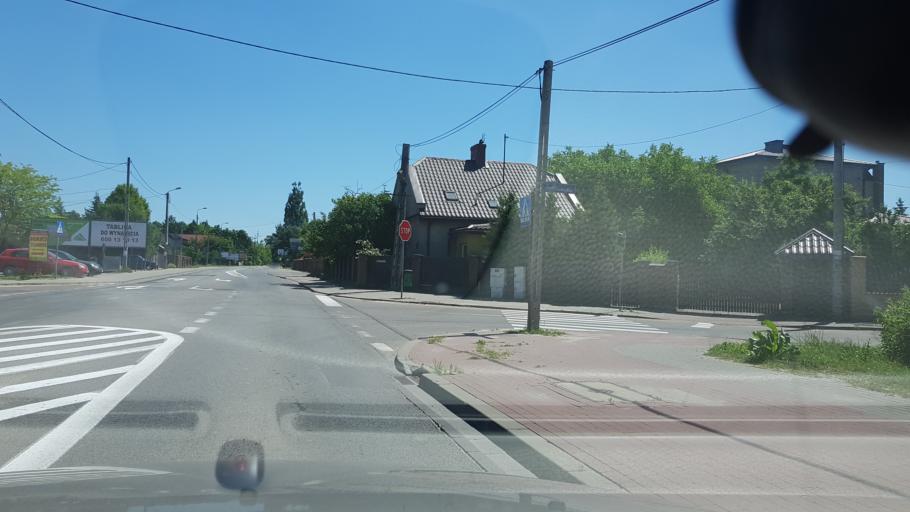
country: PL
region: Masovian Voivodeship
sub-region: Powiat wolominski
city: Marki
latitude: 52.3123
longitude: 21.1301
